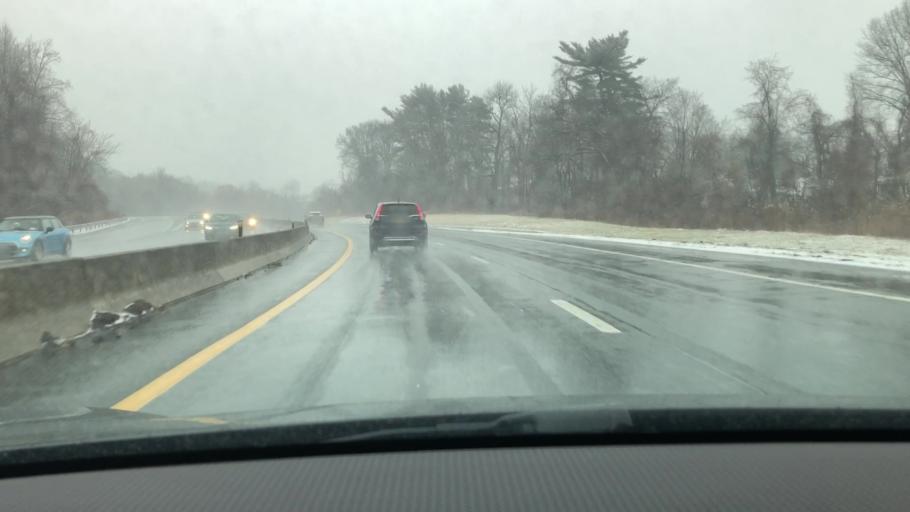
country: US
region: New York
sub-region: Westchester County
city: Tuckahoe
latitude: 40.9513
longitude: -73.7980
